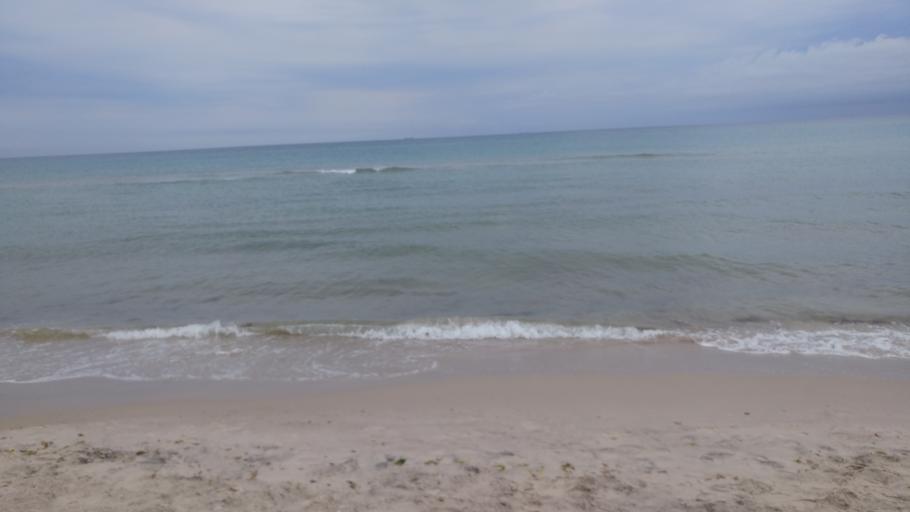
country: DK
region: North Denmark
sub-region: Frederikshavn Kommune
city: Skagen
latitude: 57.7476
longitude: 10.6476
